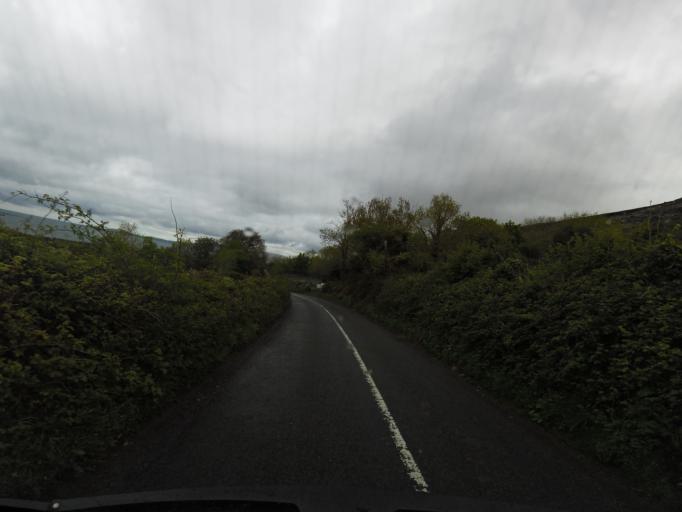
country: IE
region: Connaught
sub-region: County Galway
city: Bearna
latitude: 53.1343
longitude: -9.2083
